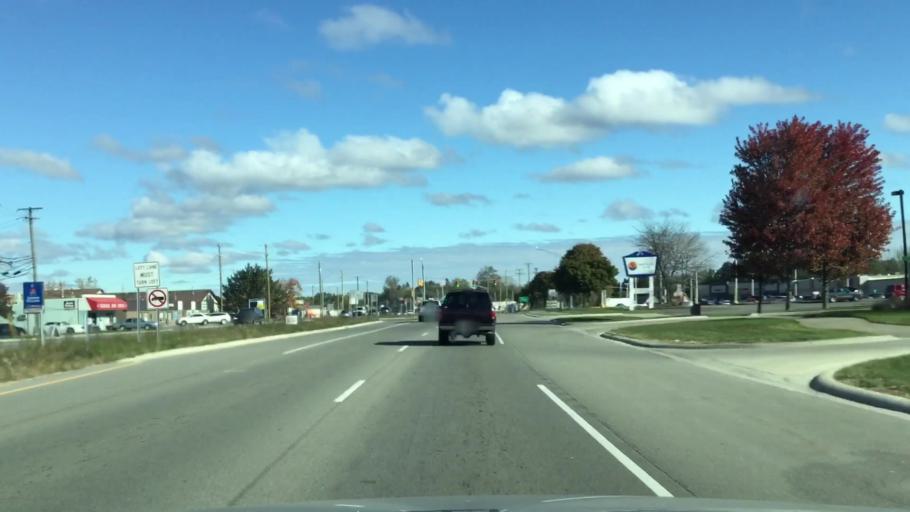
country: US
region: Michigan
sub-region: Oakland County
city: Lake Orion
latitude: 42.7648
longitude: -83.2414
